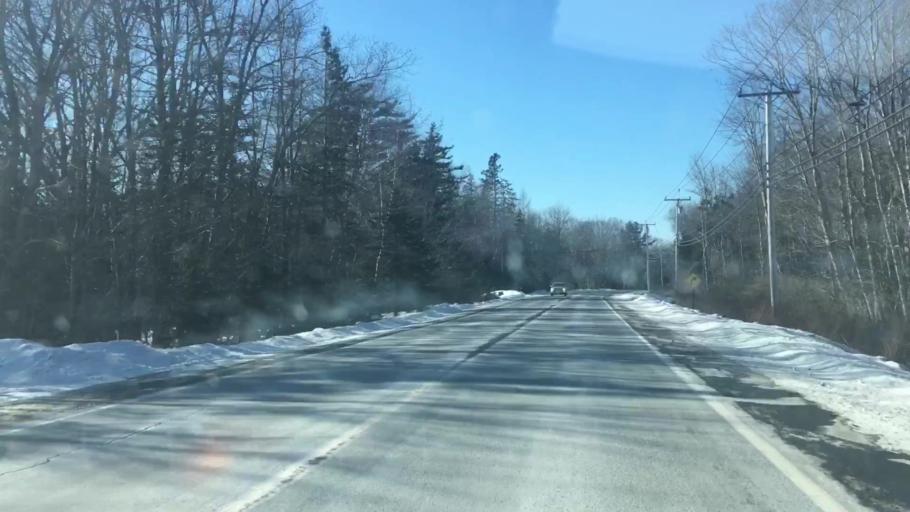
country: US
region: Maine
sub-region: Hancock County
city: Surry
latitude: 44.4930
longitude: -68.4570
